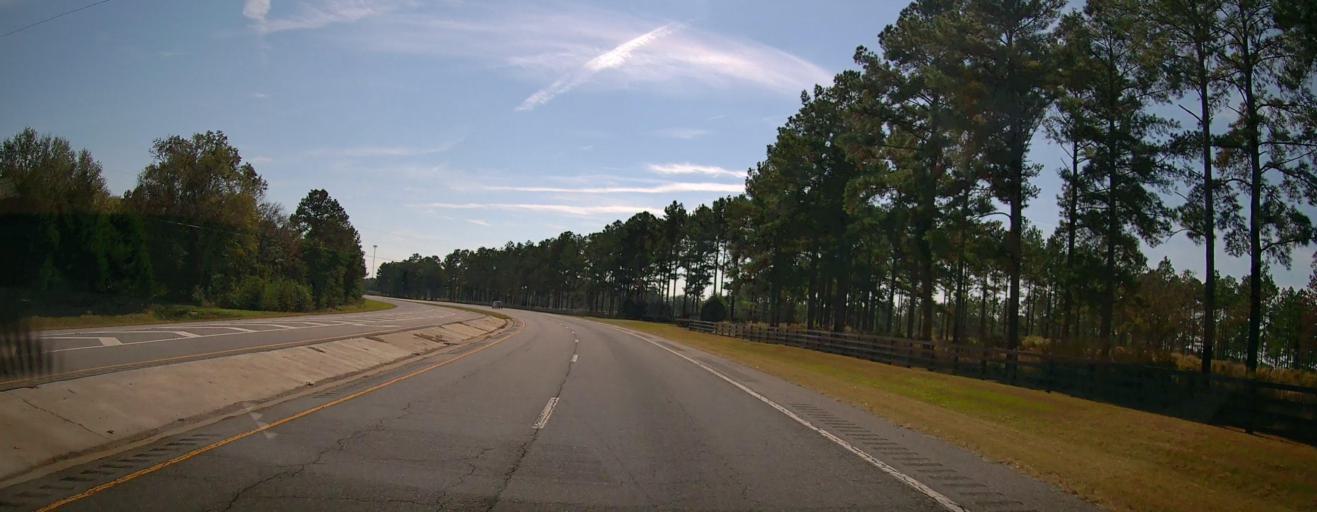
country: US
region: Georgia
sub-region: Lee County
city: Leesburg
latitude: 31.7517
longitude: -83.9874
